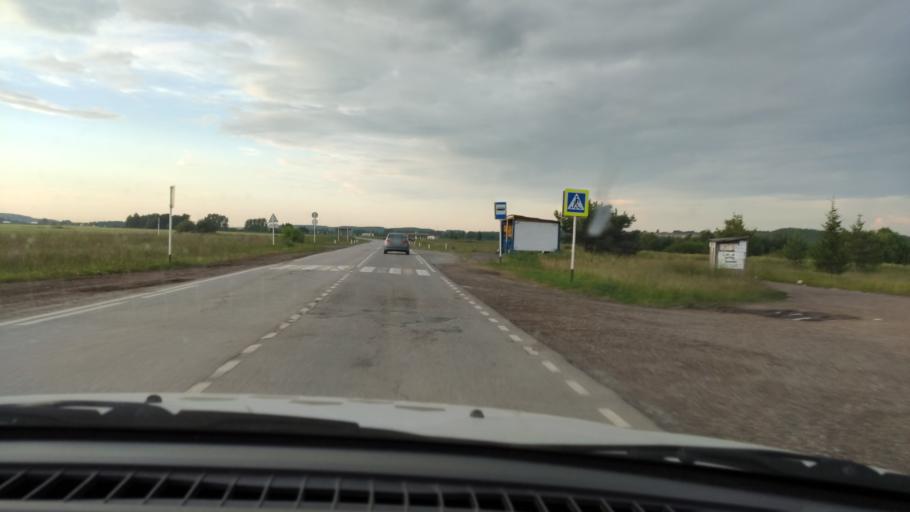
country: RU
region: Perm
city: Kukushtan
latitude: 57.4977
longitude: 56.6446
